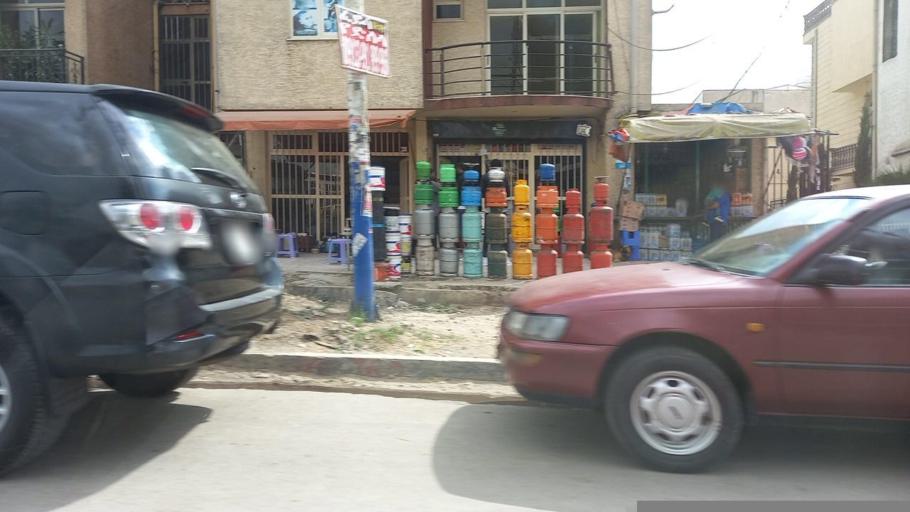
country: ET
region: Adis Abeba
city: Addis Ababa
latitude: 9.0097
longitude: 38.8589
